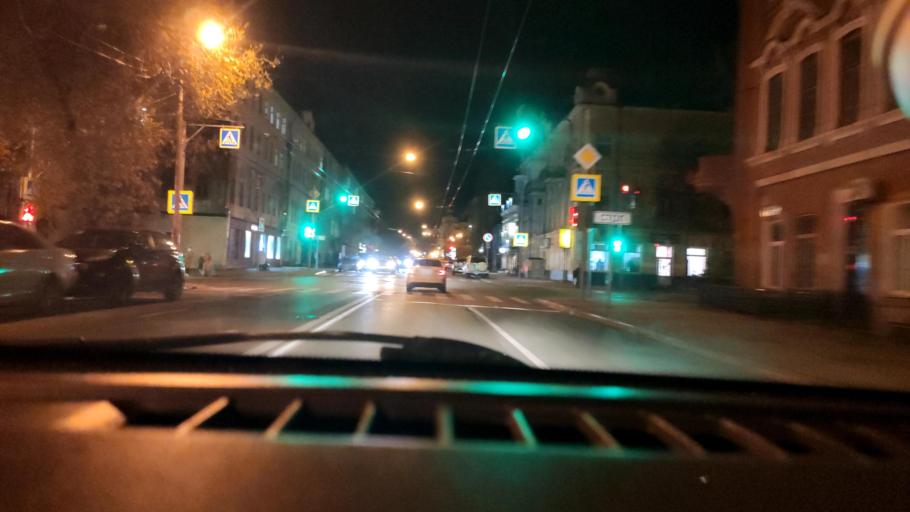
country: RU
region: Samara
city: Samara
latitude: 53.1846
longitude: 50.1029
